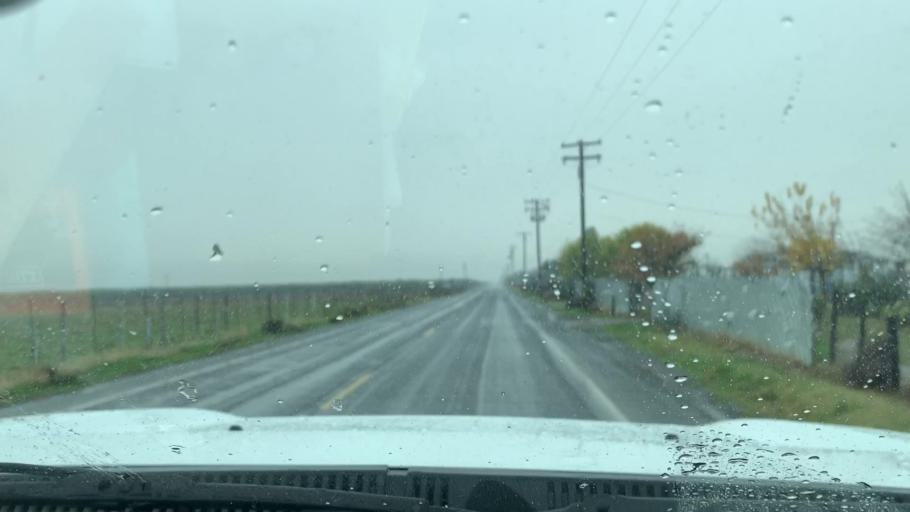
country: US
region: California
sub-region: Tulare County
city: Earlimart
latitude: 35.8919
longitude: -119.3183
